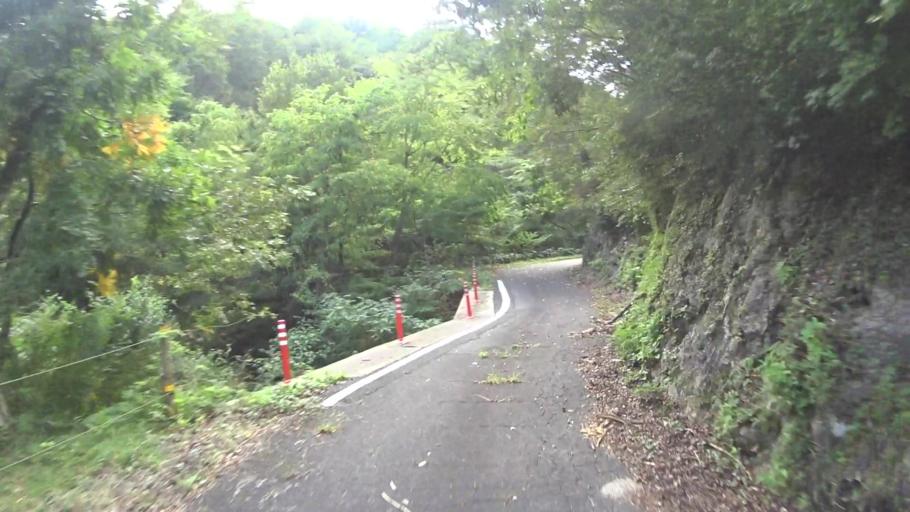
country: JP
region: Kyoto
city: Miyazu
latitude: 35.6680
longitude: 135.1395
